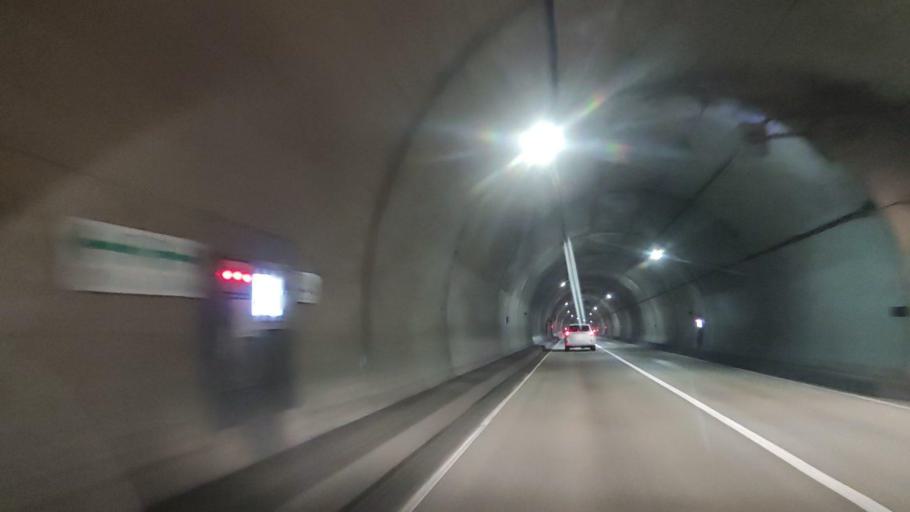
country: JP
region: Hokkaido
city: Ishikari
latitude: 43.5298
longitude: 141.3936
